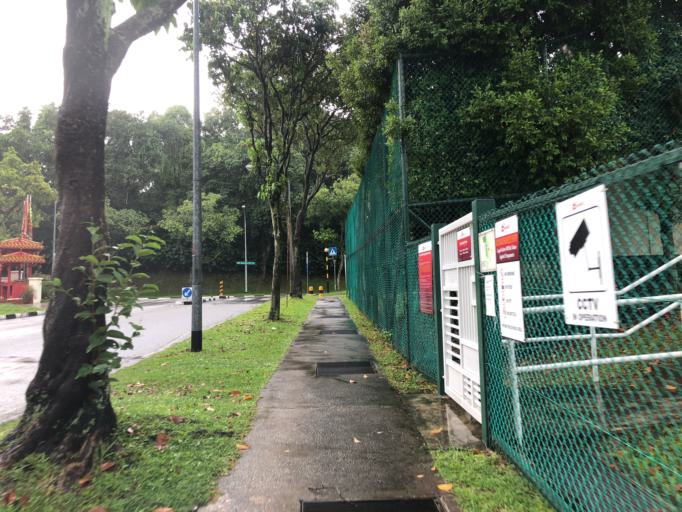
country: SG
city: Singapore
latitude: 1.3458
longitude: 103.7513
